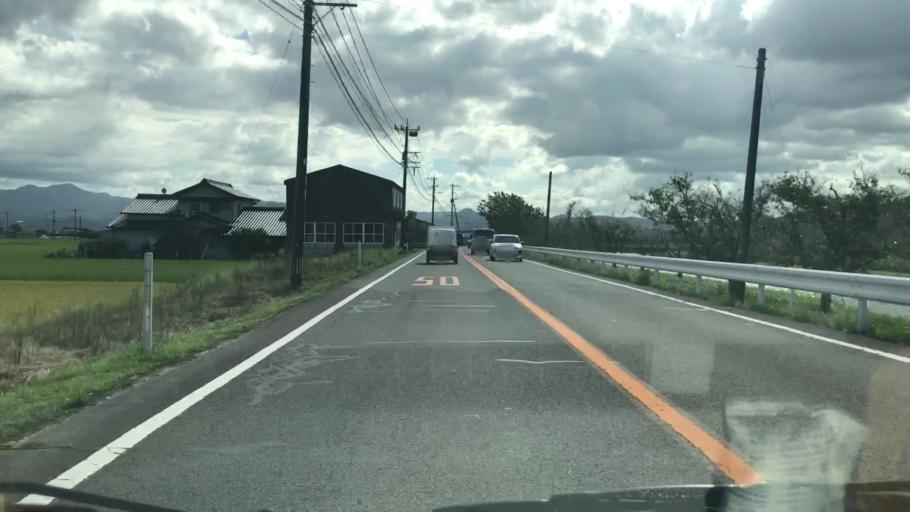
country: JP
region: Saga Prefecture
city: Kashima
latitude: 33.1564
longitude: 130.1596
